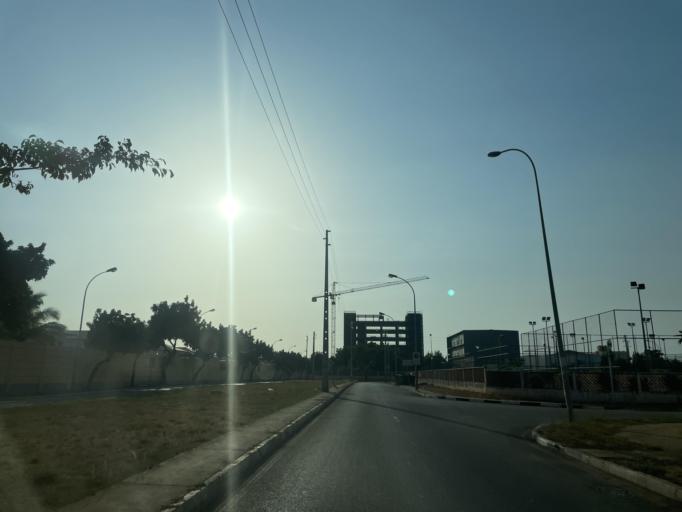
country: AO
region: Luanda
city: Luanda
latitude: -8.9151
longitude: 13.1841
